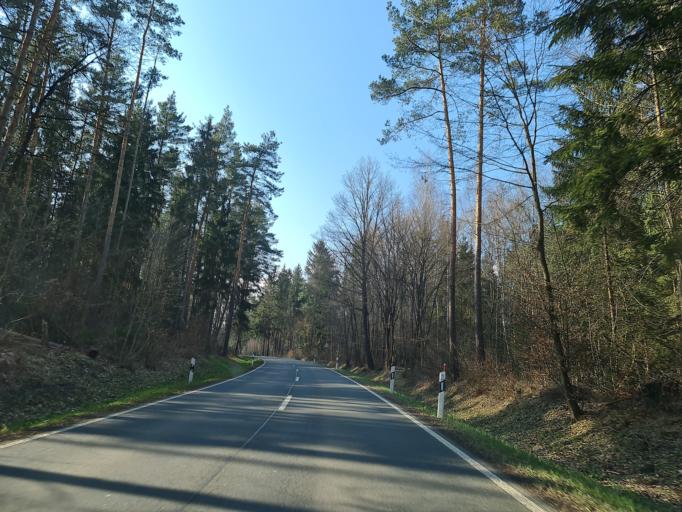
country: DE
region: Thuringia
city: Bad Klosterlausnitz
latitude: 50.9280
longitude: 11.8659
